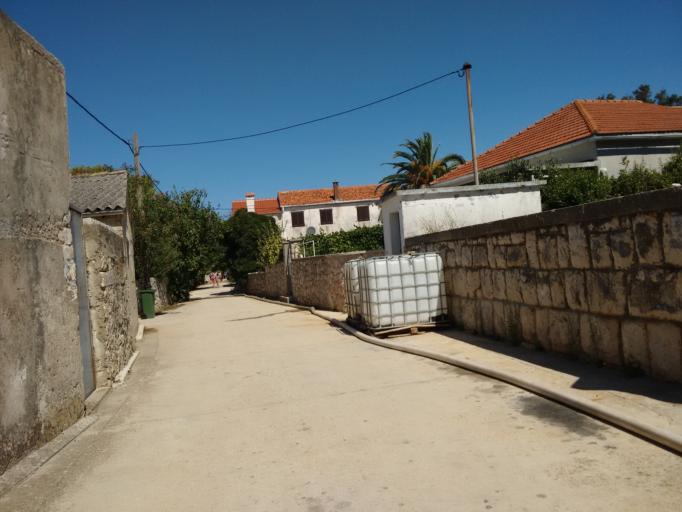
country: HR
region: Licko-Senjska
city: Novalja
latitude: 44.3768
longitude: 14.6940
